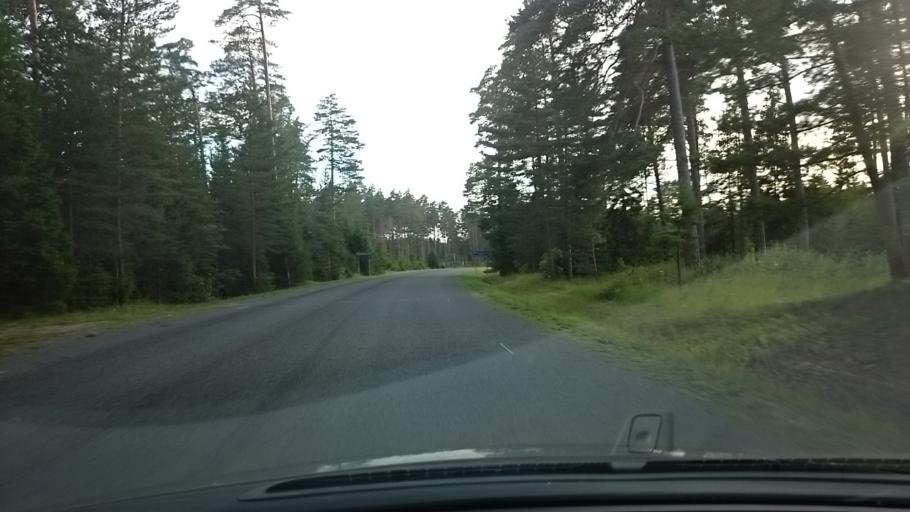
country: EE
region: Saare
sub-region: Kuressaare linn
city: Kuressaare
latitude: 58.4207
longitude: 22.1712
